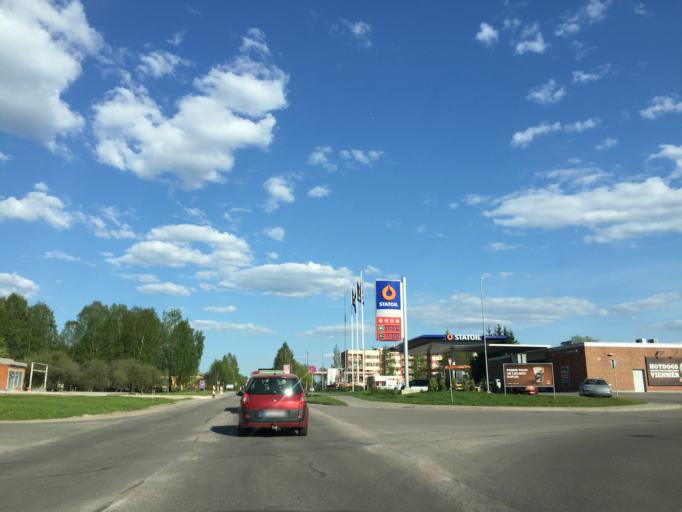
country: LV
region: Limbazu Rajons
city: Limbazi
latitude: 57.5129
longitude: 24.7269
